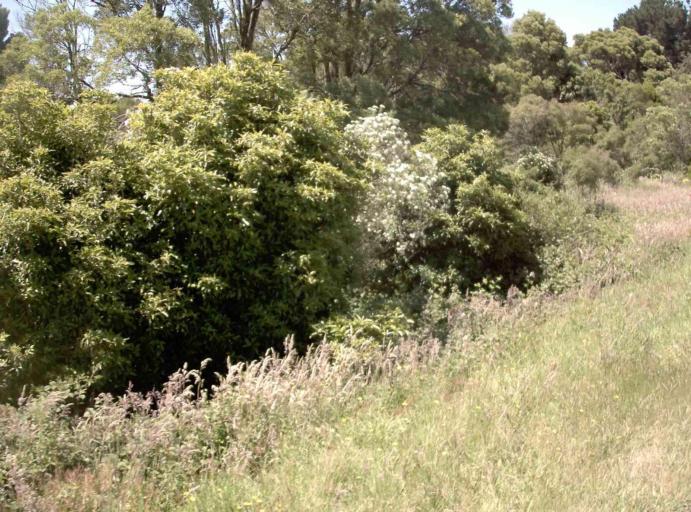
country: AU
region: Victoria
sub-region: Latrobe
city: Morwell
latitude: -38.6905
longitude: 146.1432
